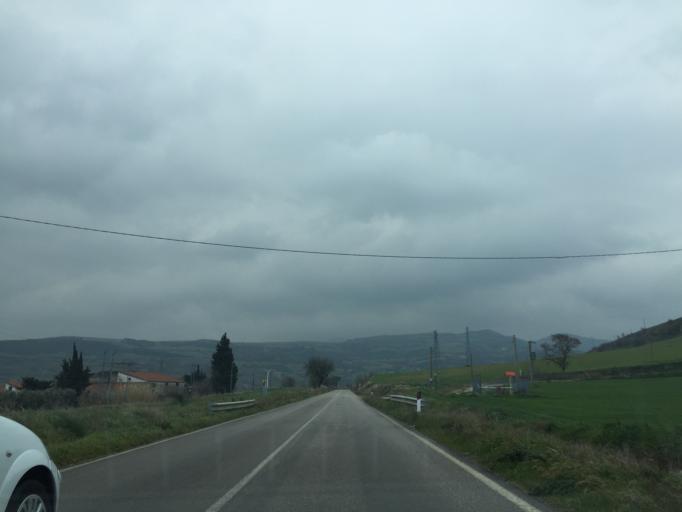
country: IT
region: Apulia
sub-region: Provincia di Foggia
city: Bovino
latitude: 41.2862
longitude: 15.3794
